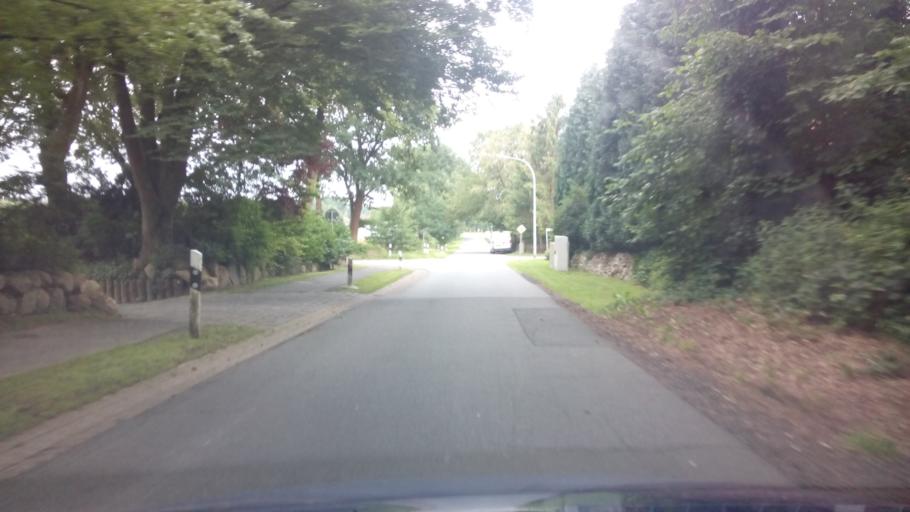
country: DE
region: Lower Saxony
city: Hambergen
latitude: 53.3004
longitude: 8.8314
